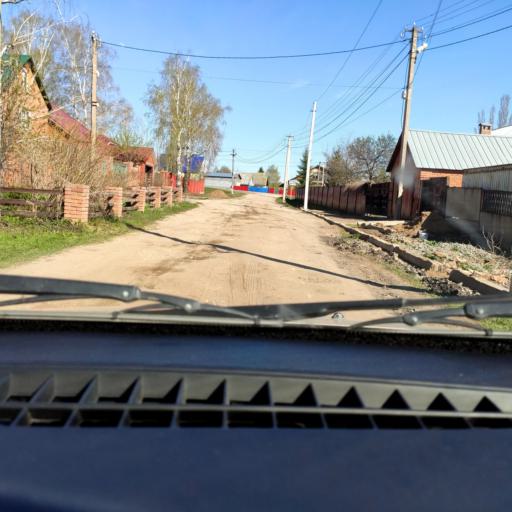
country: RU
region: Bashkortostan
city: Kabakovo
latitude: 54.5936
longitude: 56.1758
